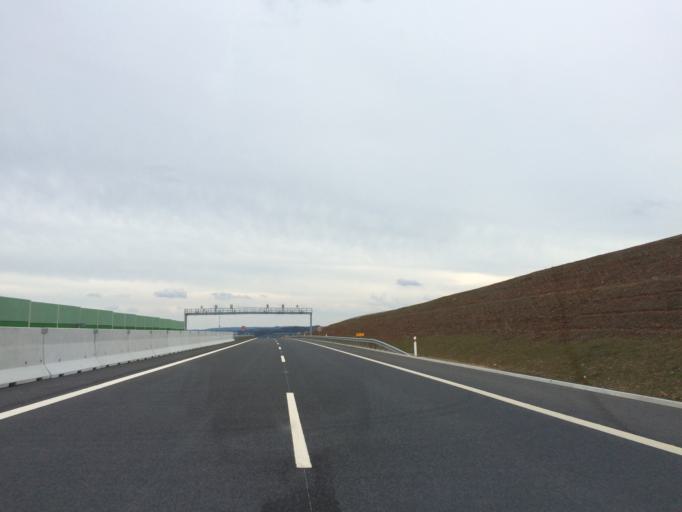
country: CZ
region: Ustecky
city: Lubenec
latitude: 50.1328
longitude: 13.2689
